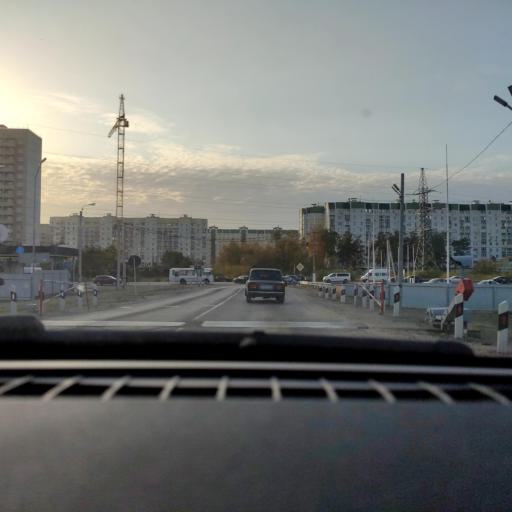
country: RU
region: Voronezj
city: Maslovka
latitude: 51.5908
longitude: 39.2498
